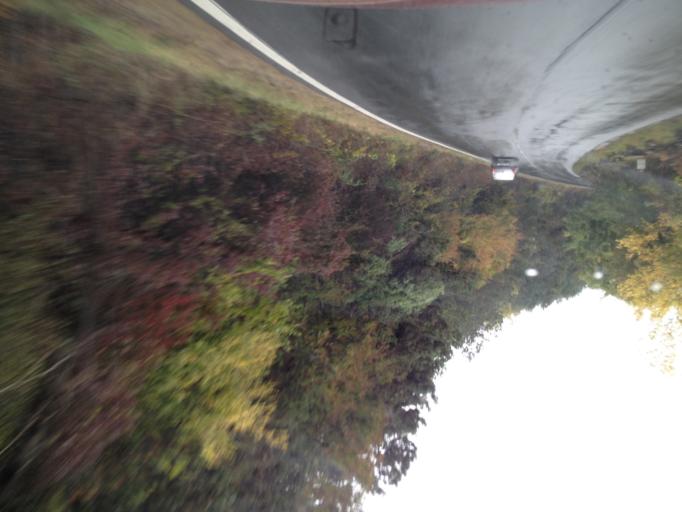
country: RO
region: Arges
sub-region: Comuna Stoenesti
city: Stoenesti
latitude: 45.2990
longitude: 25.1486
